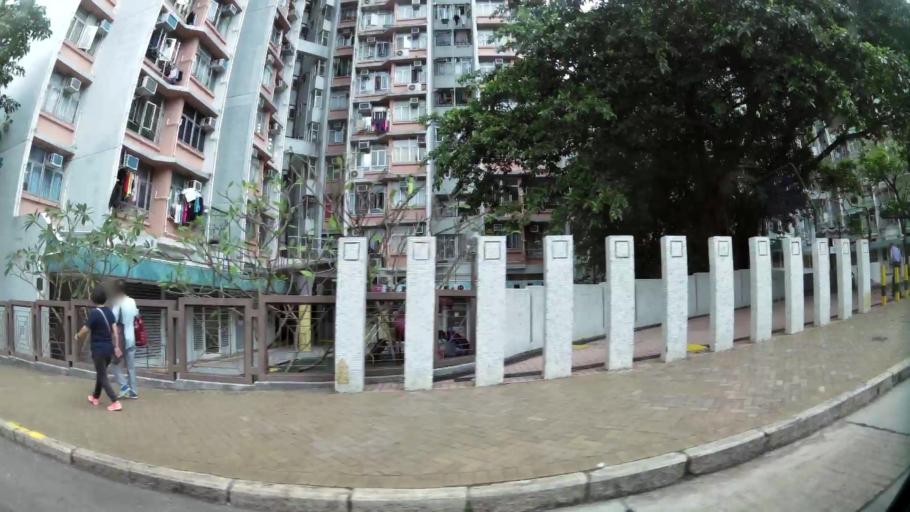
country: HK
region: Wong Tai Sin
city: Wong Tai Sin
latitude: 22.3365
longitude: 114.1873
